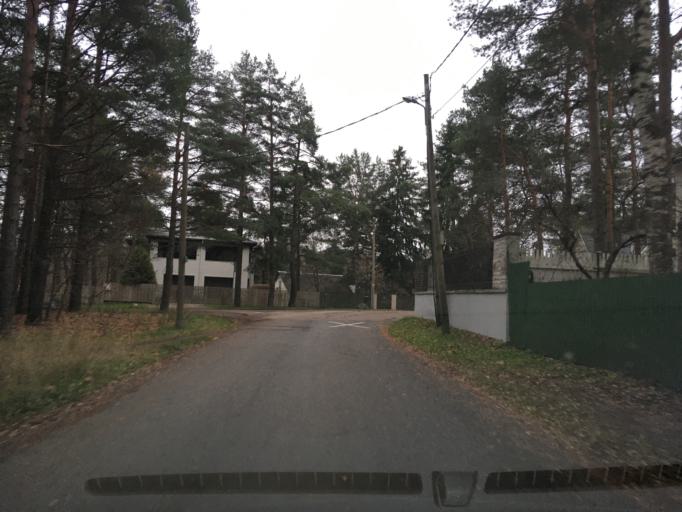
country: EE
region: Harju
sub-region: Saku vald
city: Saku
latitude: 59.3725
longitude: 24.6992
